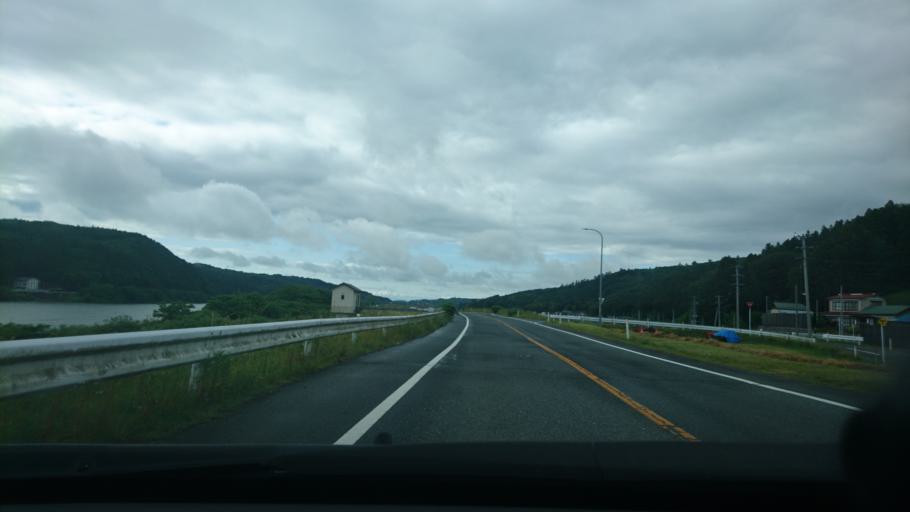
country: JP
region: Miyagi
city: Wakuya
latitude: 38.6236
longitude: 141.2955
